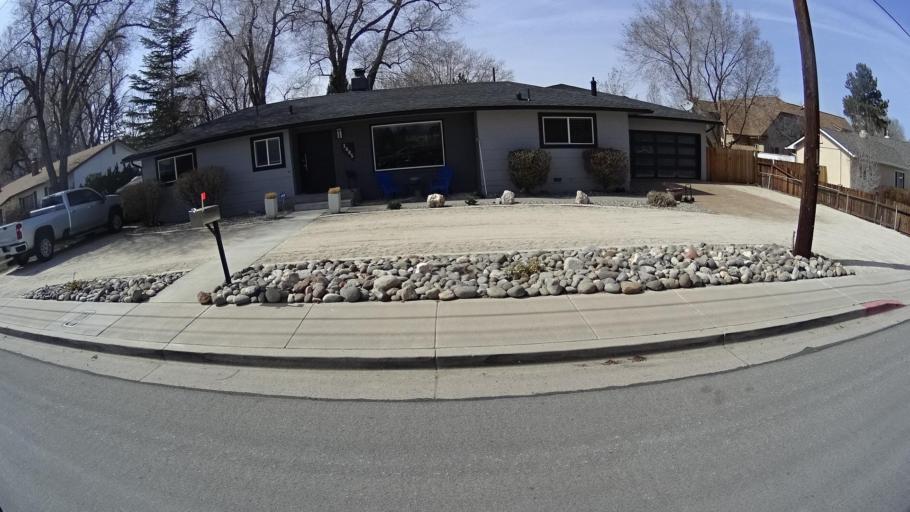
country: US
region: Nevada
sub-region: Washoe County
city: Reno
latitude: 39.5063
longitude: -119.8359
